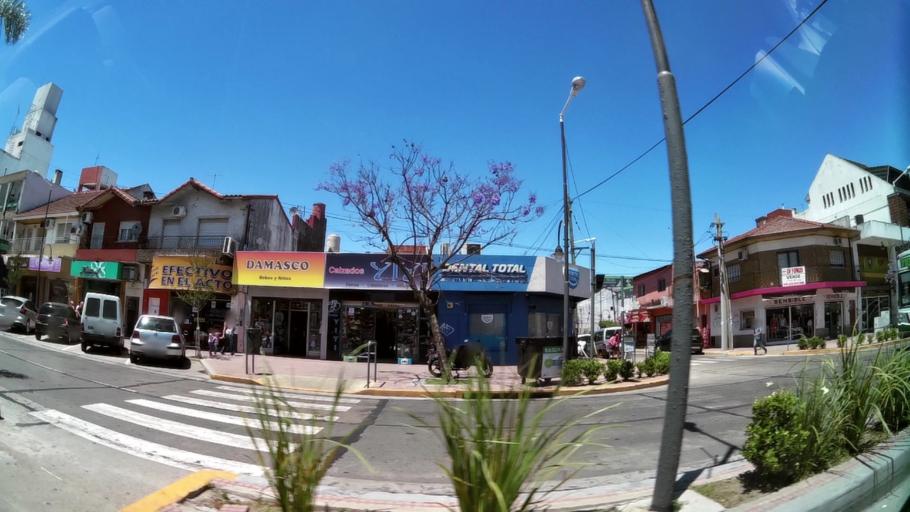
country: AR
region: Buenos Aires
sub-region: Partido de Tigre
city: Tigre
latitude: -34.4513
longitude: -58.5536
